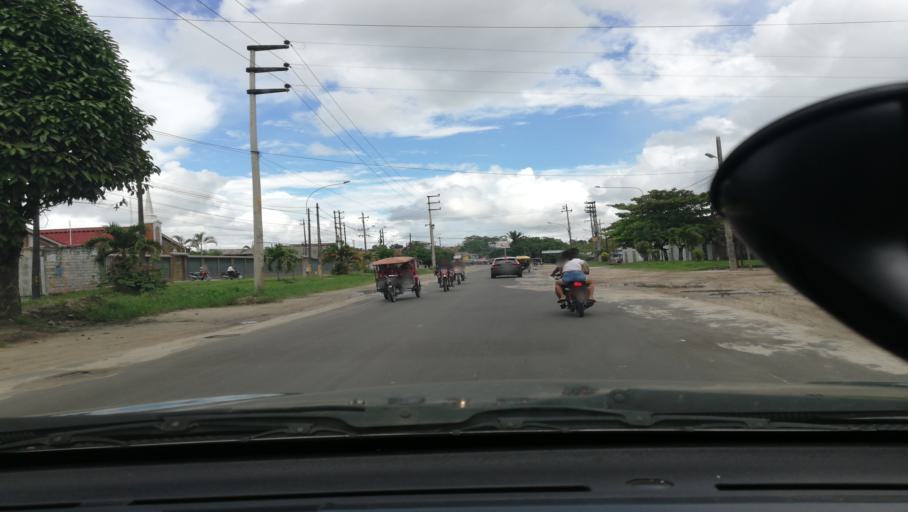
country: PE
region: Loreto
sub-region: Provincia de Maynas
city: Iquitos
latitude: -3.7869
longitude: -73.2998
